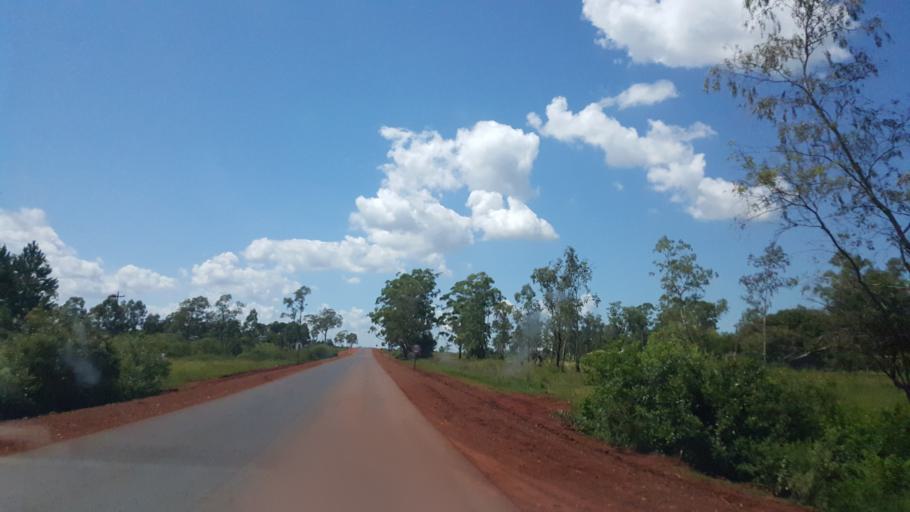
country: AR
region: Corrientes
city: Santo Tome
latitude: -28.5150
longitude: -56.0587
